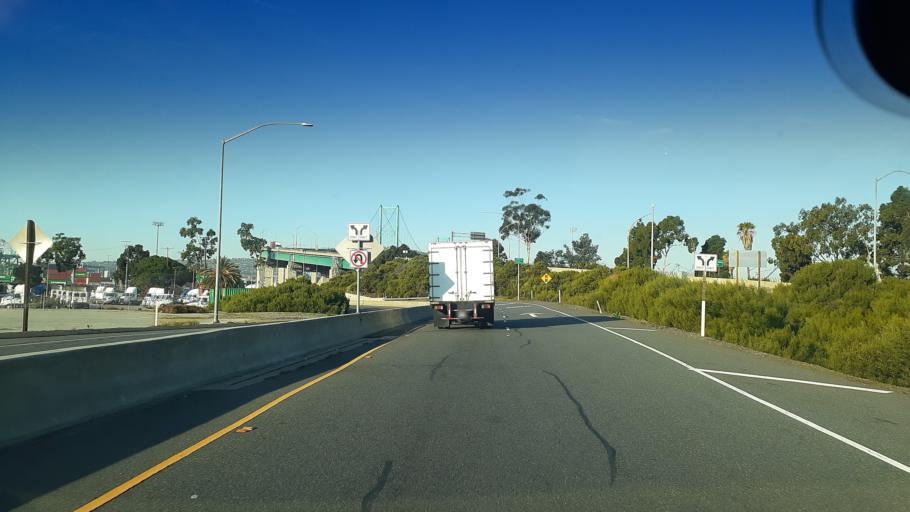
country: US
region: California
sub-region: Los Angeles County
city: San Pedro
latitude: 33.7494
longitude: -118.2597
